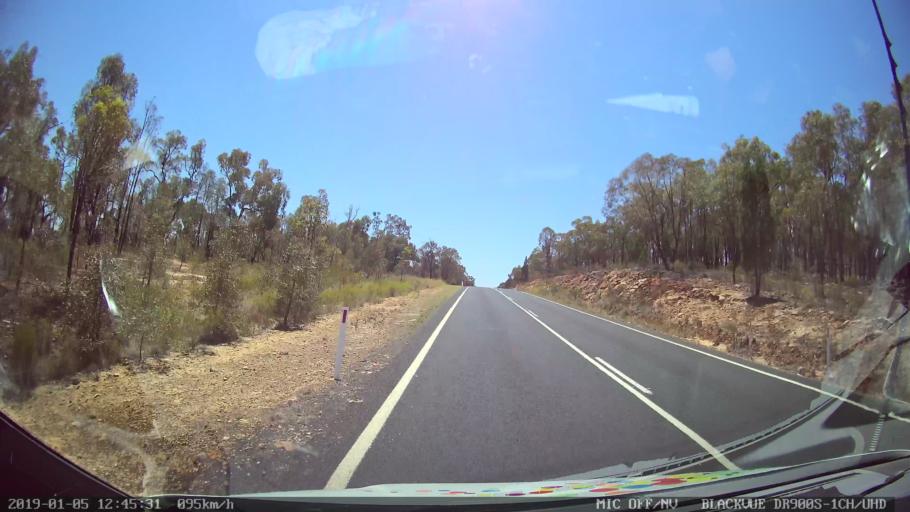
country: AU
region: New South Wales
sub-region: Warrumbungle Shire
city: Coonabarabran
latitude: -31.1270
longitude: 149.5510
